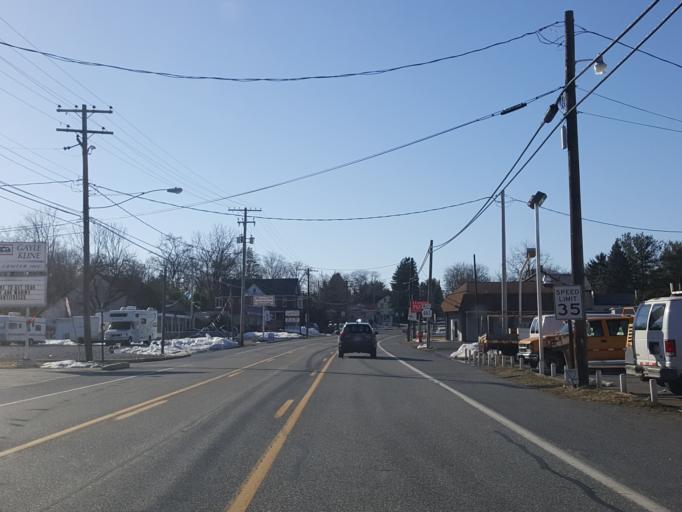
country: US
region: Pennsylvania
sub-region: Lancaster County
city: Mountville
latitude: 40.0374
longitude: -76.4187
